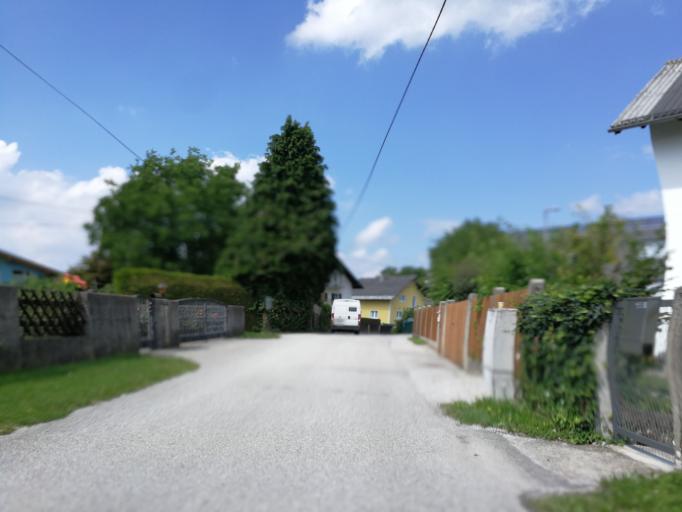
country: AT
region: Salzburg
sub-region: Politischer Bezirk Salzburg-Umgebung
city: Bergheim
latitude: 47.8195
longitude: 13.0088
